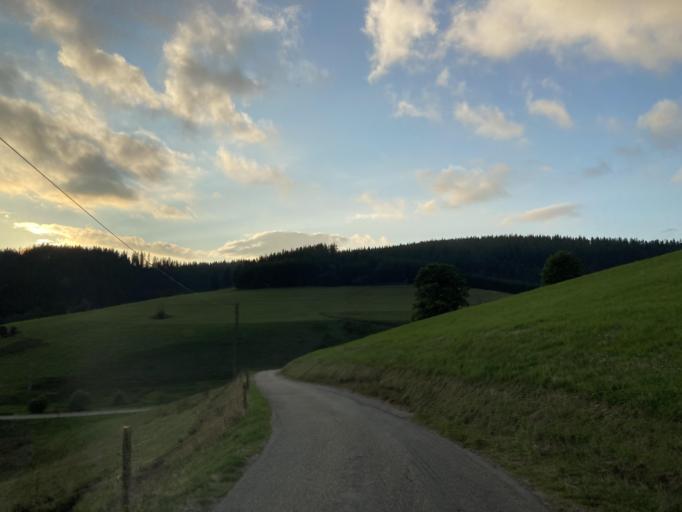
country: DE
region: Baden-Wuerttemberg
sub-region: Freiburg Region
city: Vohrenbach
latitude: 48.0818
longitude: 8.2757
